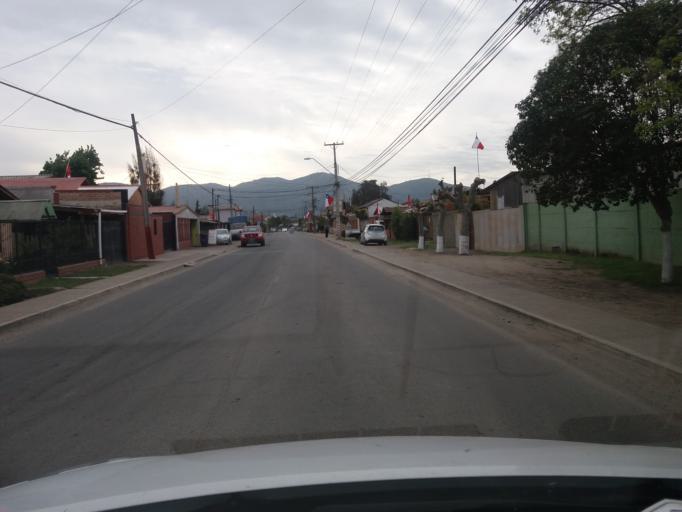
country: CL
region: Valparaiso
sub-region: Provincia de Quillota
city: Hacienda La Calera
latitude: -32.7809
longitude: -71.1823
